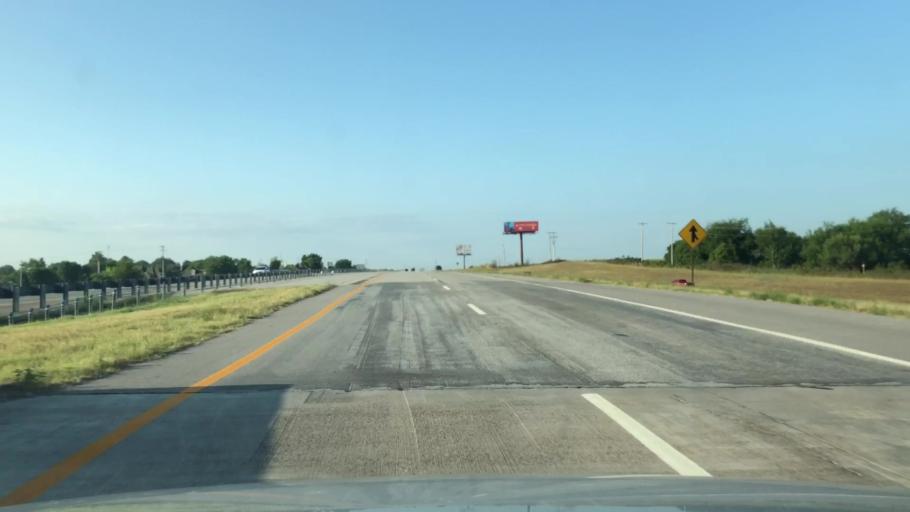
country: US
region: Oklahoma
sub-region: Osage County
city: Skiatook
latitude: 36.3654
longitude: -95.9208
